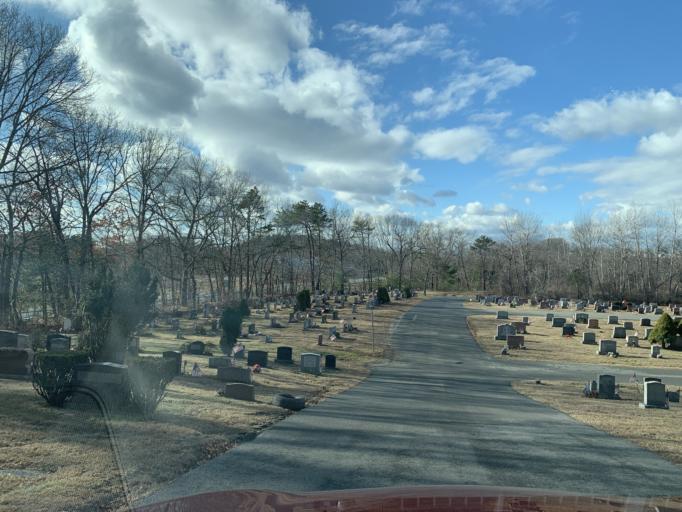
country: US
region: Massachusetts
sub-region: Essex County
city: Amesbury
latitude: 42.8414
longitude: -70.9329
